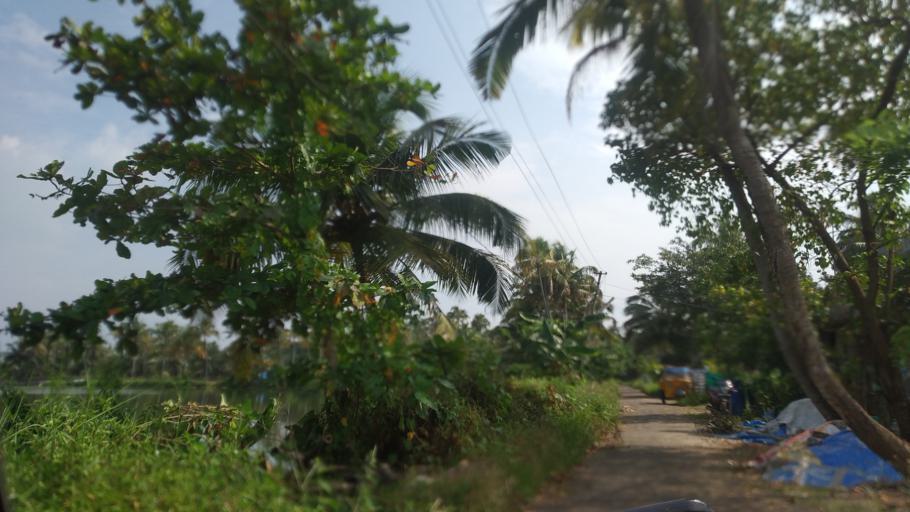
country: IN
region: Kerala
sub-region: Ernakulam
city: Elur
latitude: 10.0844
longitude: 76.2190
